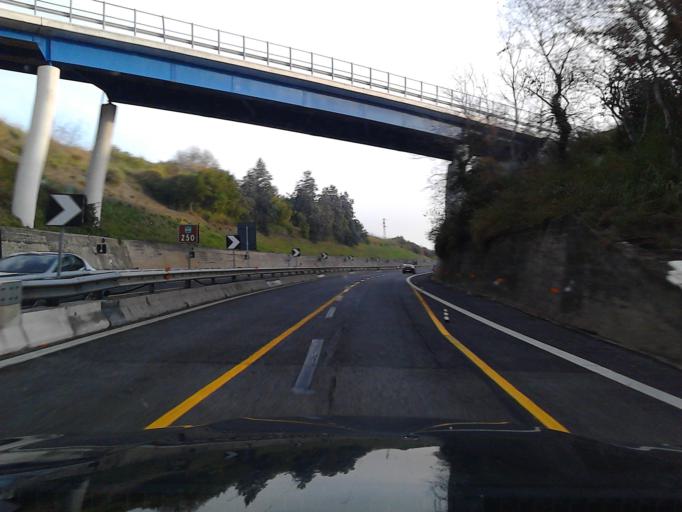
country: IT
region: Abruzzo
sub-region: Provincia di Chieti
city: Marina di San Vito
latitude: 42.3107
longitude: 14.4207
